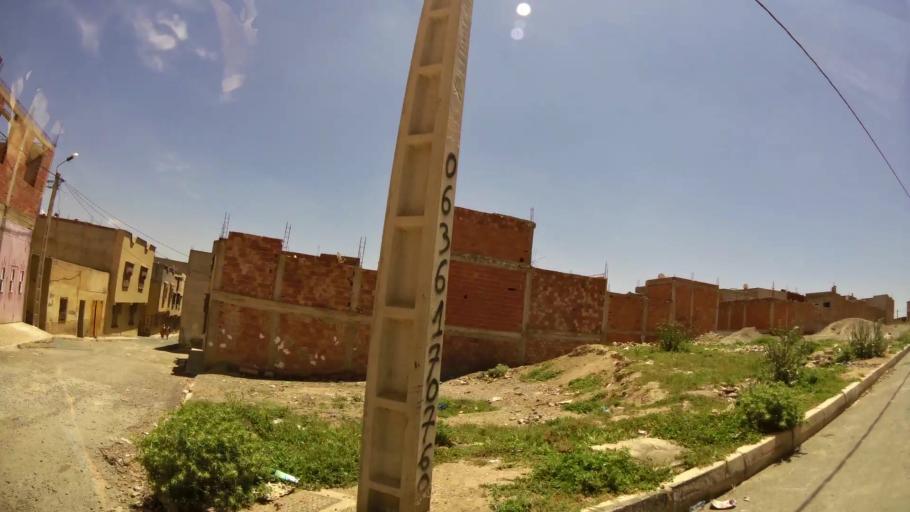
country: MA
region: Oriental
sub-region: Oujda-Angad
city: Oujda
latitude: 34.6548
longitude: -1.9364
